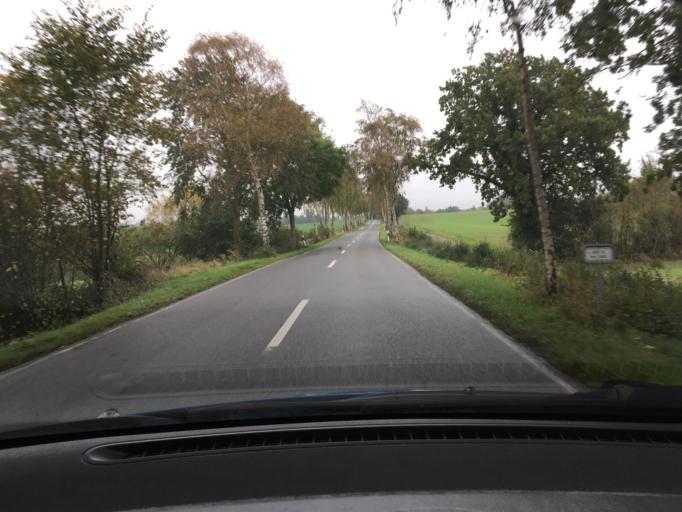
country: DE
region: Schleswig-Holstein
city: Bosau
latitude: 54.0949
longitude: 10.4647
